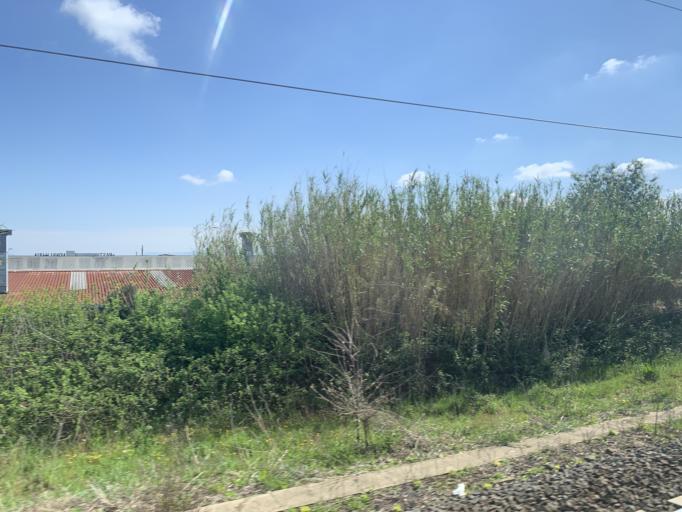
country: IT
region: Latium
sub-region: Citta metropolitana di Roma Capitale
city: Ciampino
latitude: 41.8132
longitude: 12.5866
